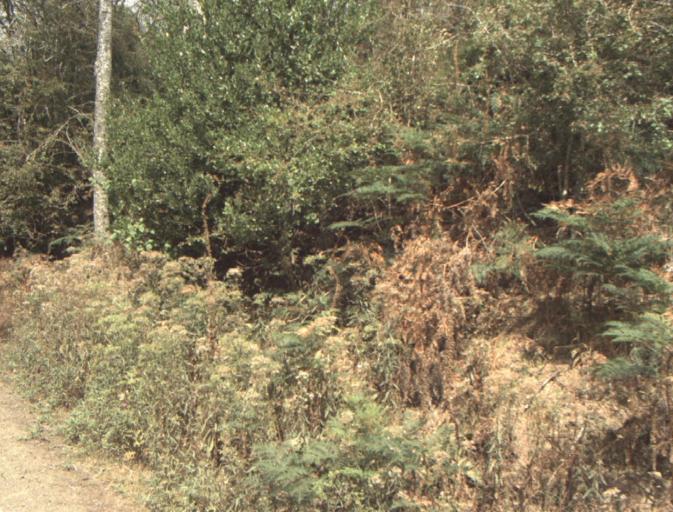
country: AU
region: Tasmania
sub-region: Dorset
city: Bridport
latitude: -41.1948
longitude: 147.2630
